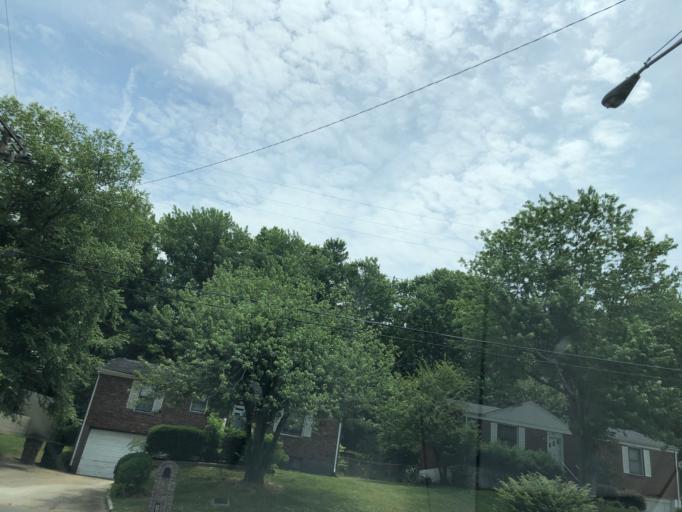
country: US
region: Tennessee
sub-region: Rutherford County
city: La Vergne
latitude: 36.0695
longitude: -86.6720
